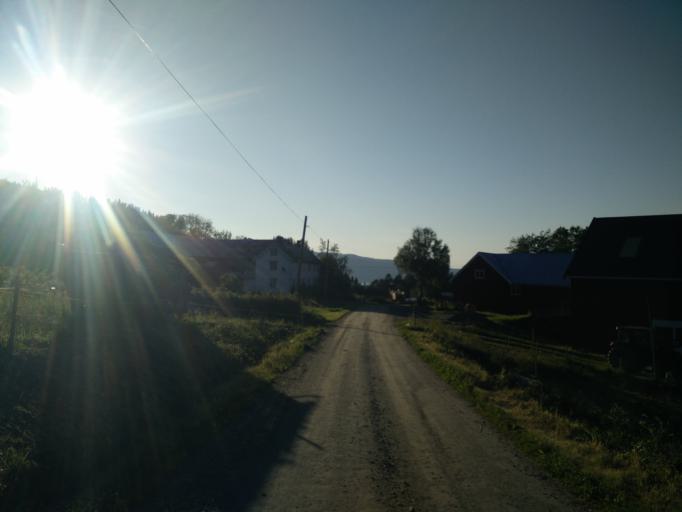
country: NO
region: Sor-Trondelag
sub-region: Skaun
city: Borsa
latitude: 63.3400
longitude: 10.0365
